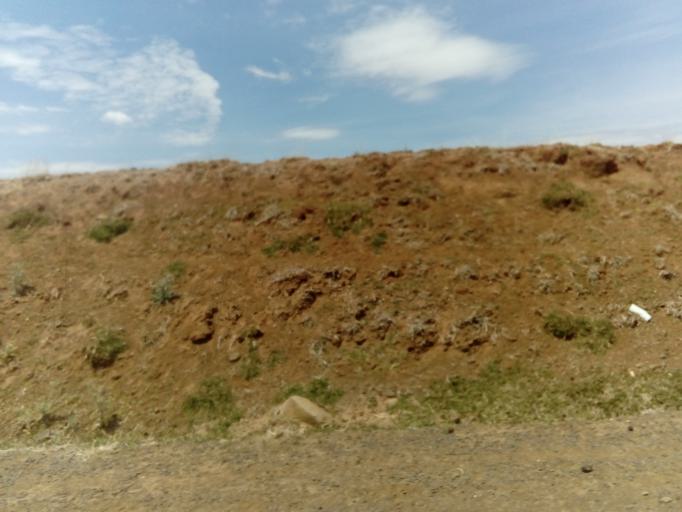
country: LS
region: Berea
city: Teyateyaneng
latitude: -29.0853
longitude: 27.9139
